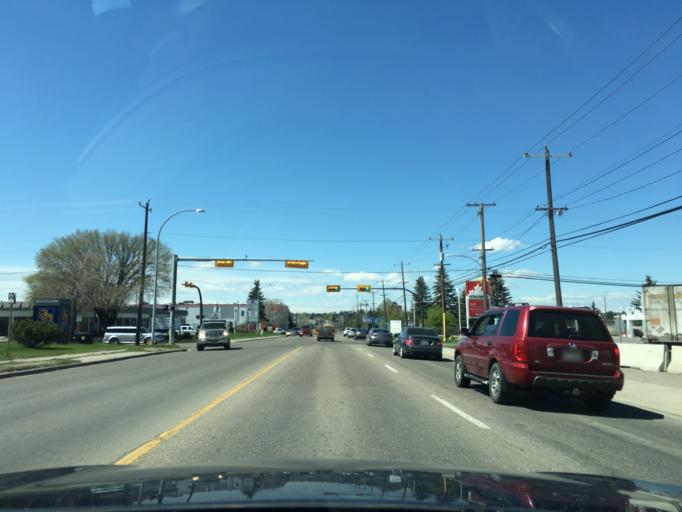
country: CA
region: Alberta
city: Calgary
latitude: 51.0014
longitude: -114.0563
